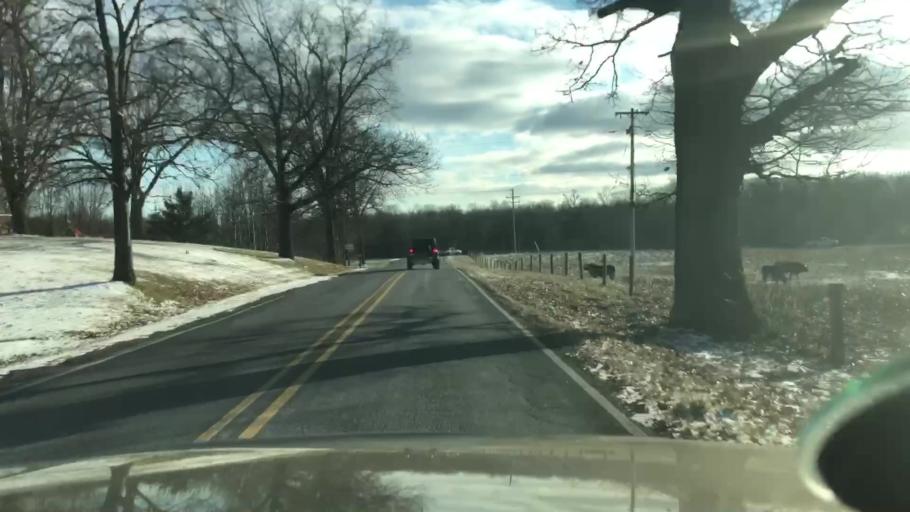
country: US
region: Michigan
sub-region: Jackson County
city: Vandercook Lake
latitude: 42.0988
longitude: -84.4511
